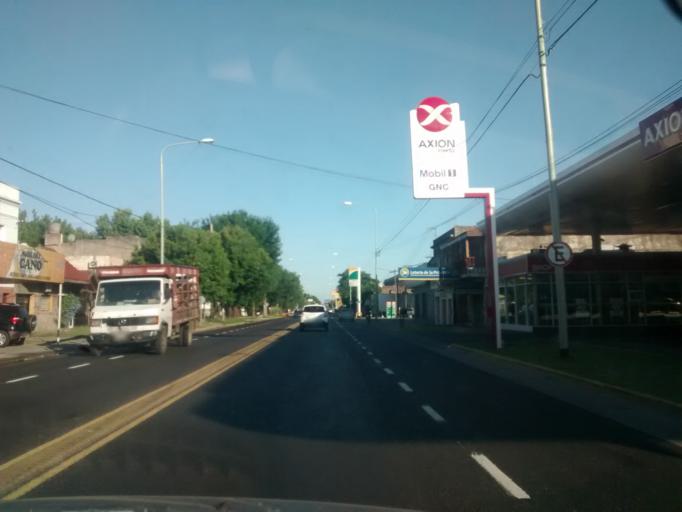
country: AR
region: Buenos Aires
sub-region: Partido de La Plata
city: La Plata
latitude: -34.8987
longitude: -57.9385
